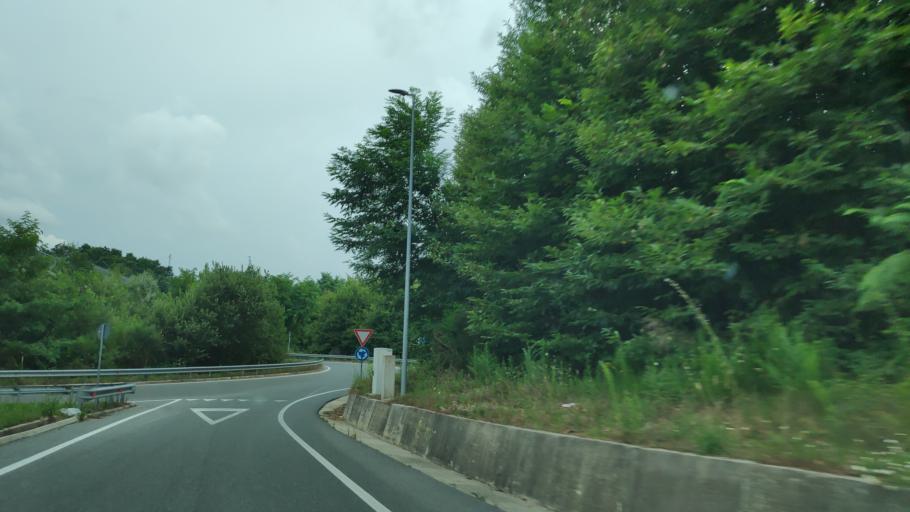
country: IT
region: Calabria
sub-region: Provincia di Vibo-Valentia
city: Spadola
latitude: 38.5932
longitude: 16.3310
